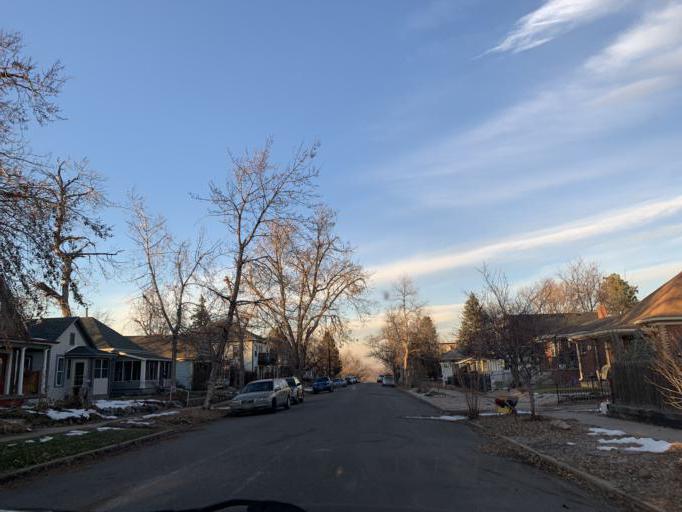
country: US
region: Colorado
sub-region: Adams County
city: Berkley
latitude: 39.7876
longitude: -105.0416
